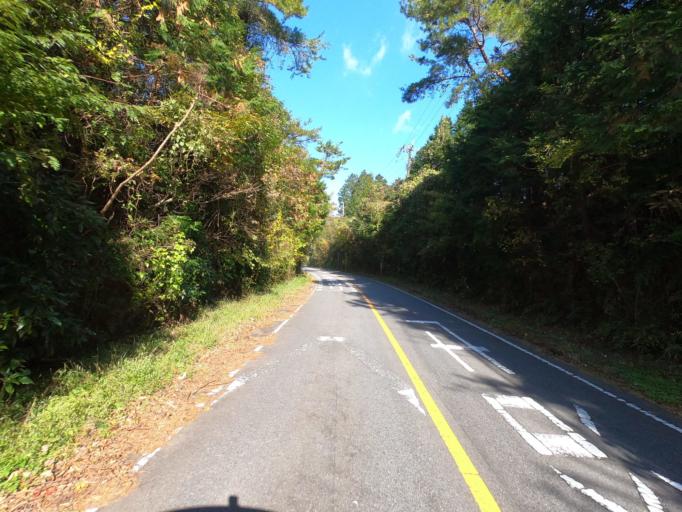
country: JP
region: Ibaraki
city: Tsukuba
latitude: 36.2124
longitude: 140.1221
